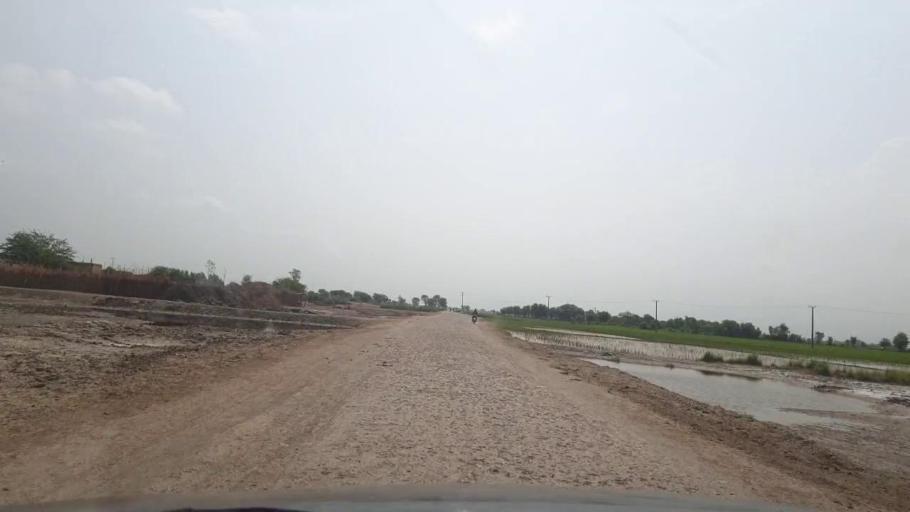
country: PK
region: Sindh
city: Ratodero
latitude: 27.8415
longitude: 68.3211
